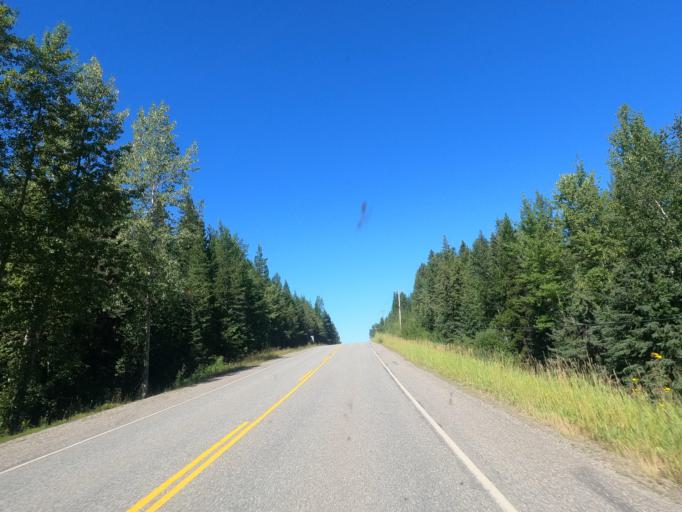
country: CA
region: British Columbia
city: Quesnel
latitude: 53.0292
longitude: -122.3914
